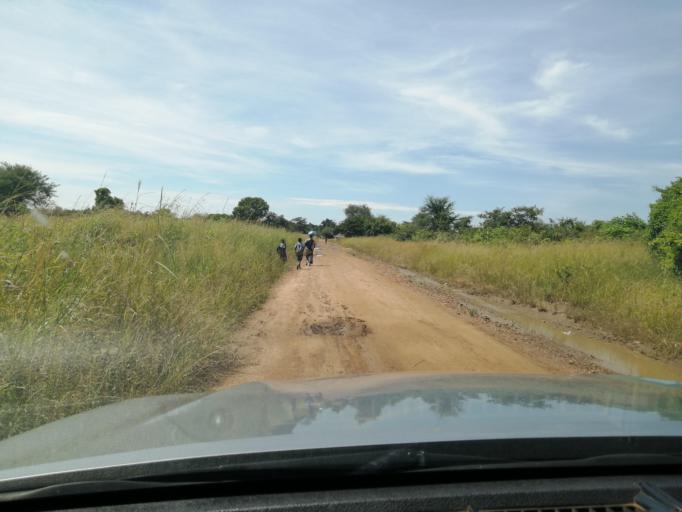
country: ZM
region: Central
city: Chibombo
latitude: -15.0000
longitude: 27.8204
